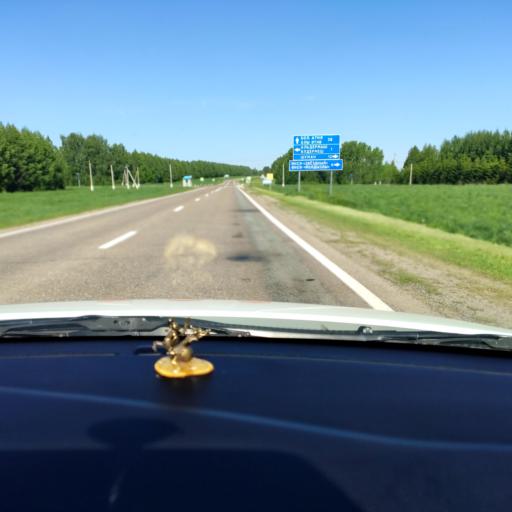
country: RU
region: Tatarstan
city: Vysokaya Gora
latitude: 56.0329
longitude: 49.2396
